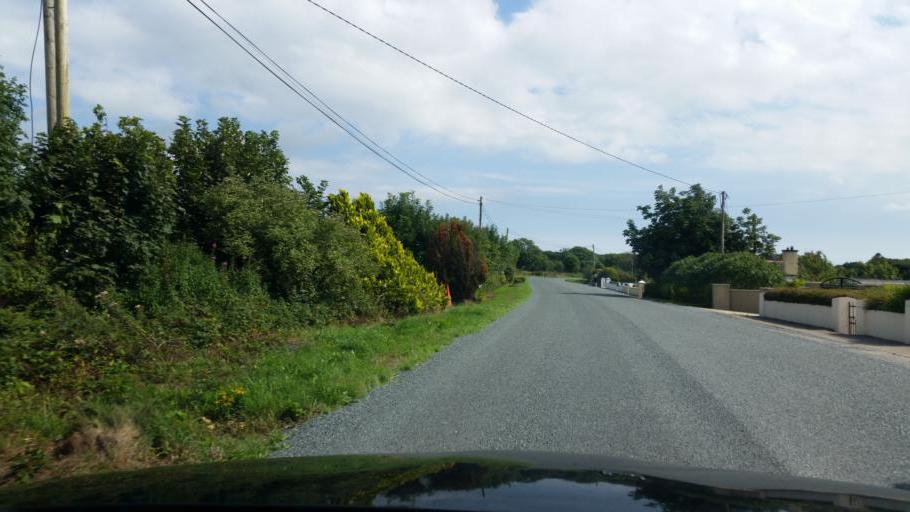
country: IE
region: Leinster
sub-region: Loch Garman
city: Loch Garman
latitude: 52.3001
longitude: -6.6439
